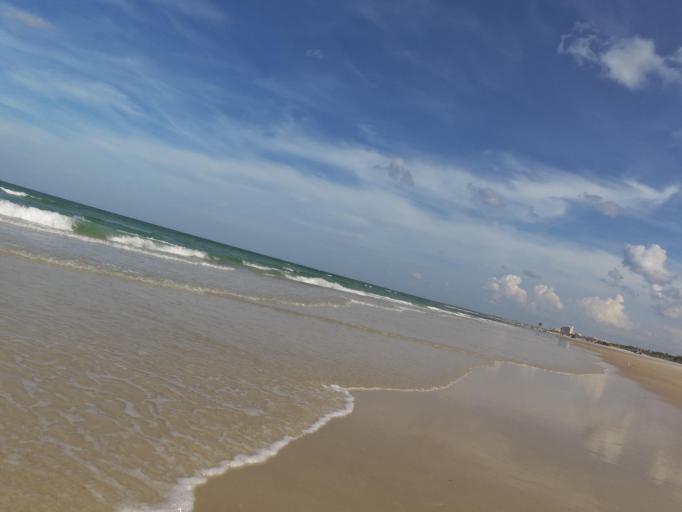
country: US
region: Florida
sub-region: Volusia County
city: Ponce Inlet
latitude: 29.0871
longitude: -80.9258
